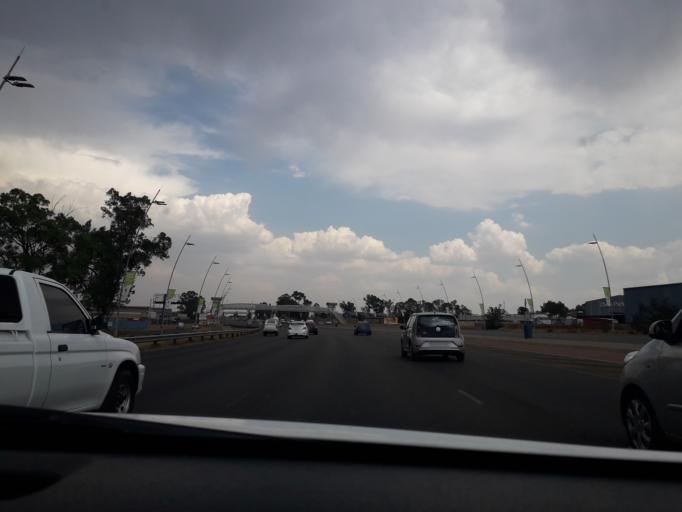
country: ZA
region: Gauteng
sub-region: City of Johannesburg Metropolitan Municipality
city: Modderfontein
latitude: -26.0719
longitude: 28.1862
